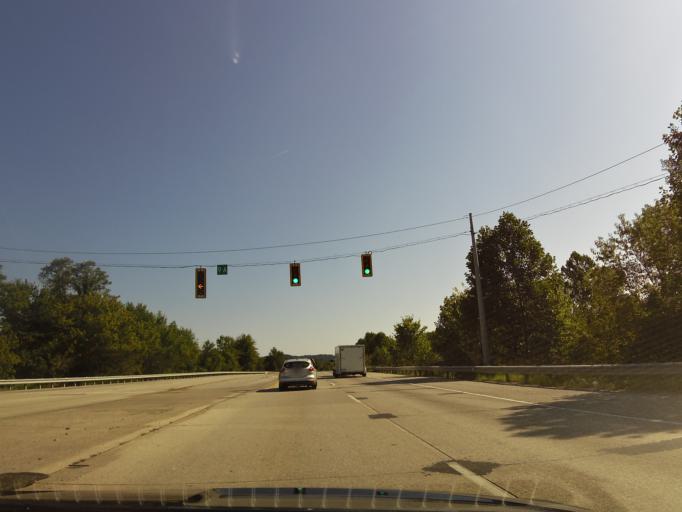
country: US
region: Kentucky
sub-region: Laurel County
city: London
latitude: 37.1149
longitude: -84.0609
